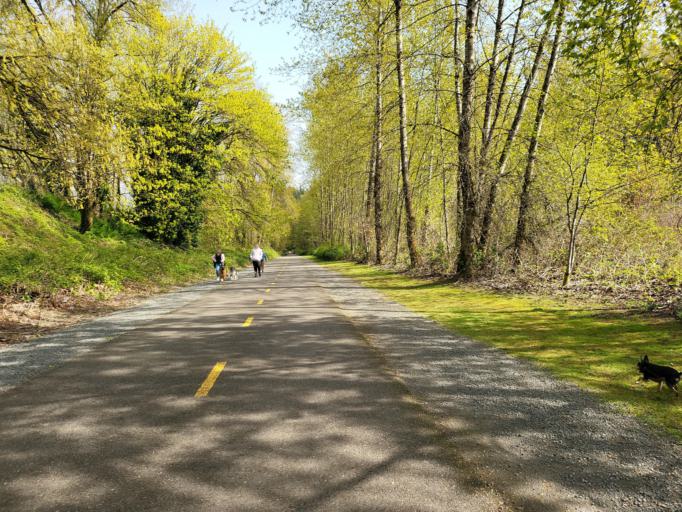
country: US
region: Washington
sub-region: King County
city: Renton
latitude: 47.4779
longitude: -122.1931
